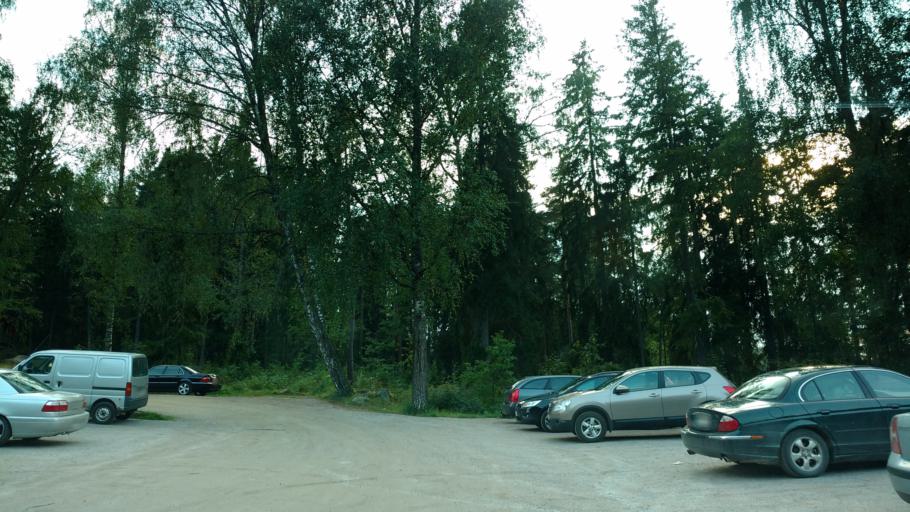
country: FI
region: Varsinais-Suomi
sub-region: Salo
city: Halikko
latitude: 60.3641
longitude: 23.0660
